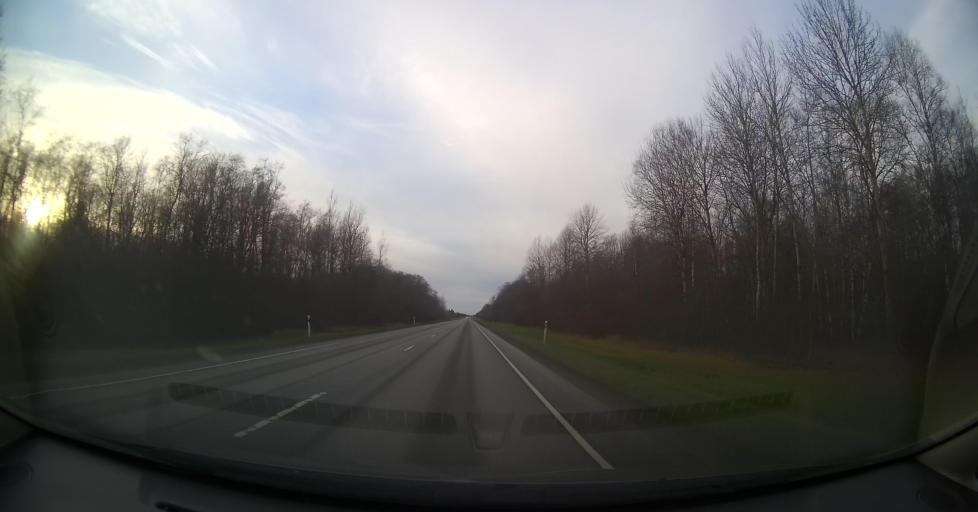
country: EE
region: Ida-Virumaa
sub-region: Sillamaee linn
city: Sillamae
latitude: 59.3920
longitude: 27.7057
